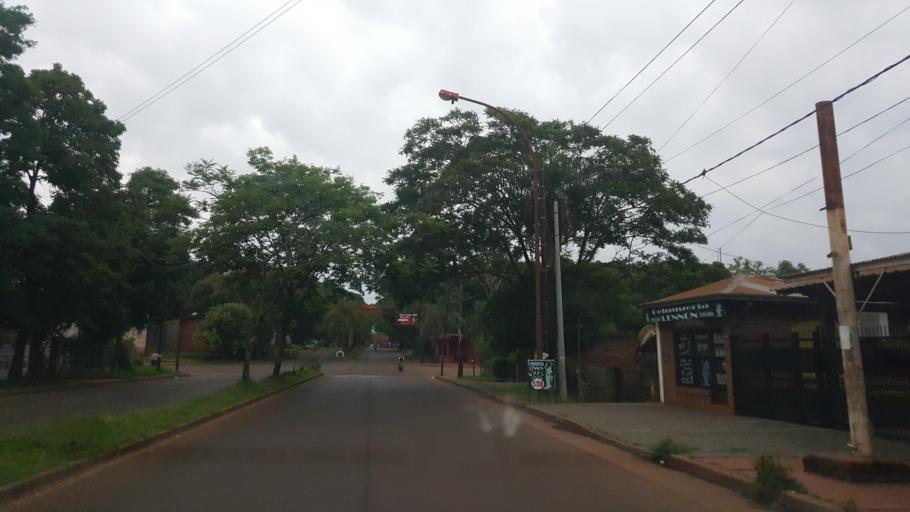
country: AR
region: Misiones
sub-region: Departamento de Capital
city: Posadas
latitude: -27.3599
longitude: -55.9307
